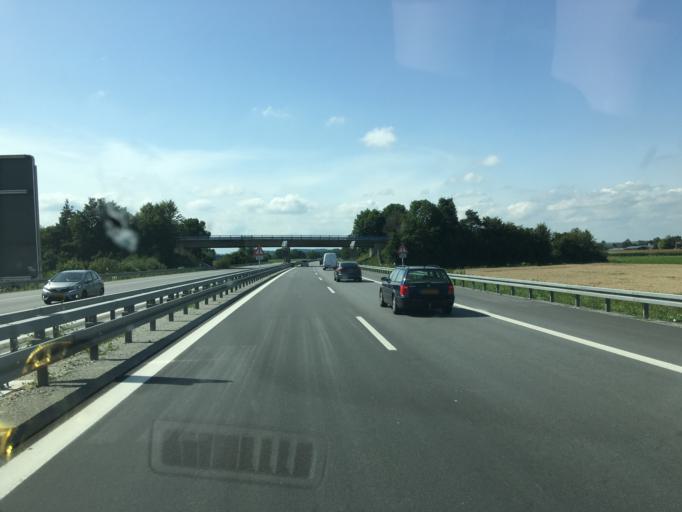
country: AT
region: Upper Austria
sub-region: Politischer Bezirk Scharding
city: Scharding
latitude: 48.4254
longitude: 13.3873
